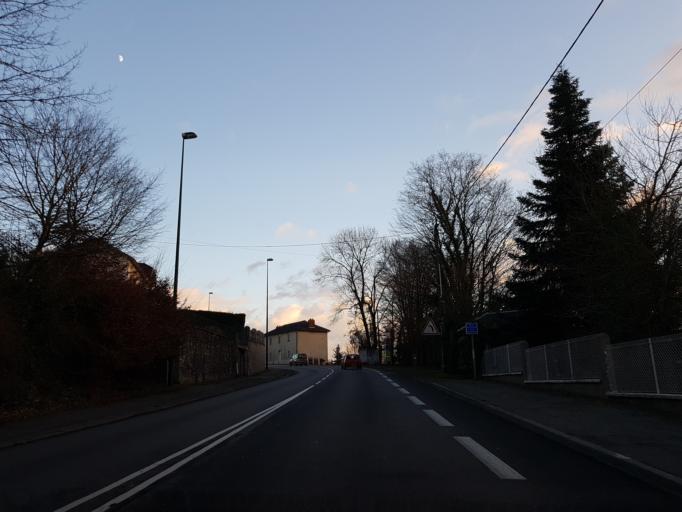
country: FR
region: Limousin
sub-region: Departement de la Haute-Vienne
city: Limoges
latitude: 45.8255
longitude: 1.2879
